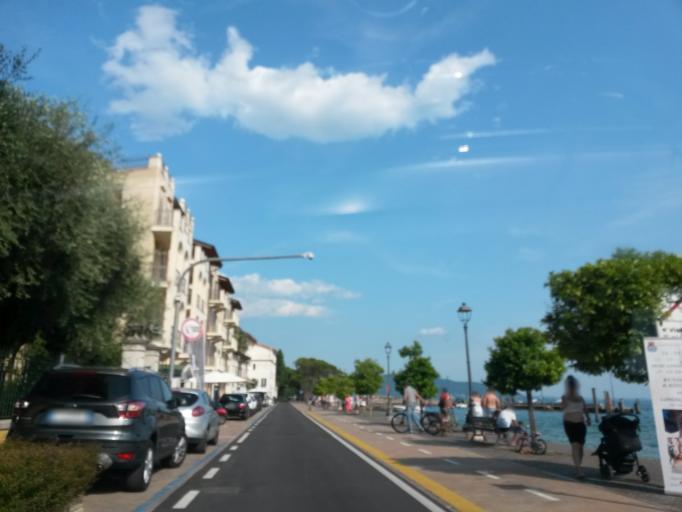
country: IT
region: Lombardy
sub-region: Provincia di Brescia
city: Toscolano Maderno
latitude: 45.6331
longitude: 10.6010
